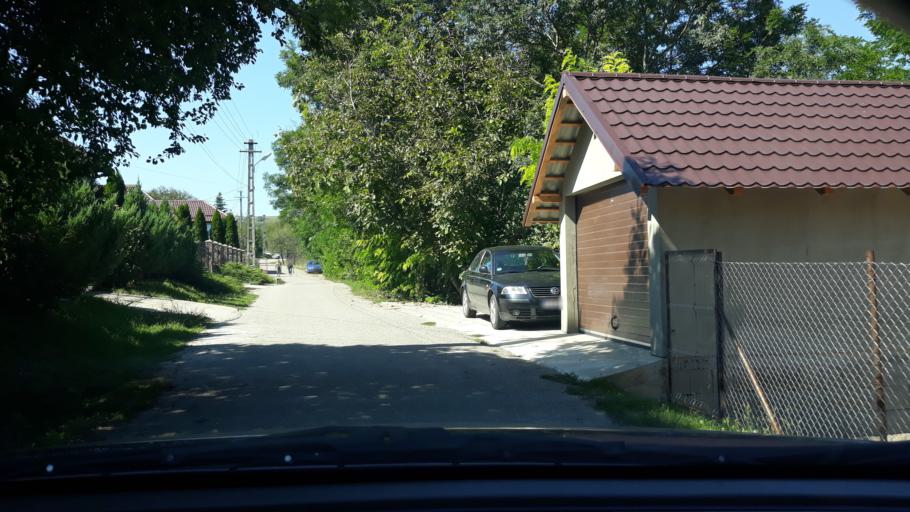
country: RO
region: Salaj
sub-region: Comuna Dobrin
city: Dobrin
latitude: 47.2937
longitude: 23.0931
